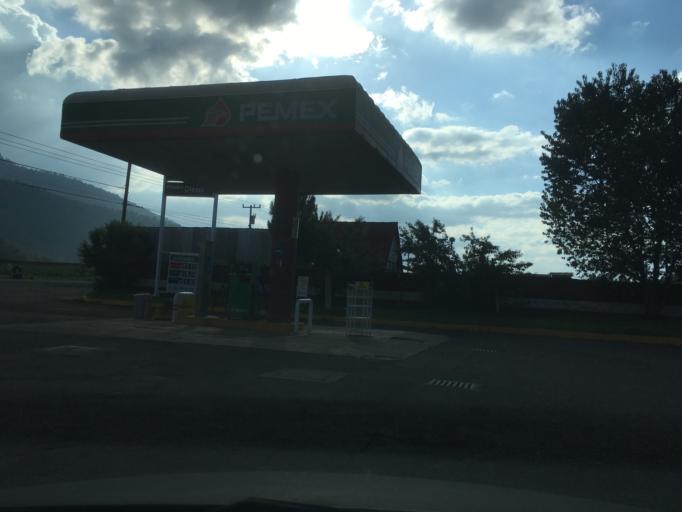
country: MX
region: Michoacan
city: Cheran
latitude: 19.6659
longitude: -101.9401
